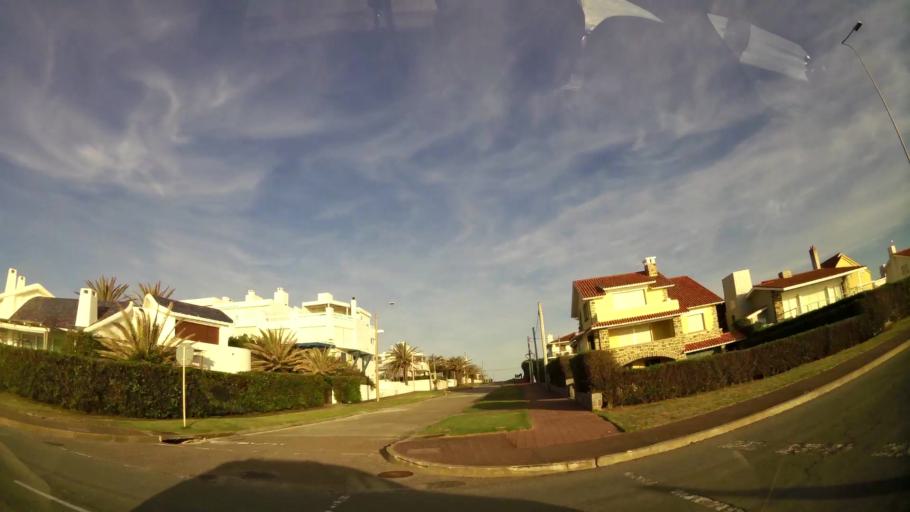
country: UY
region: Maldonado
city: Punta del Este
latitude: -34.9706
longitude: -54.9538
